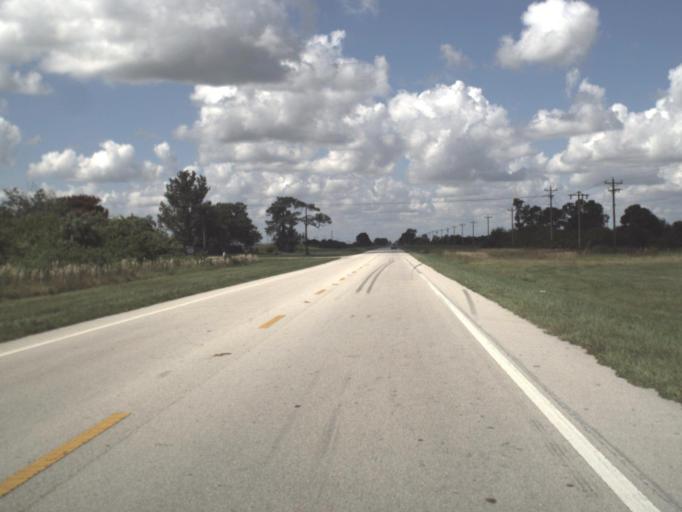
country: US
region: Florida
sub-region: Collier County
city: Immokalee
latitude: 26.4933
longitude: -81.4649
